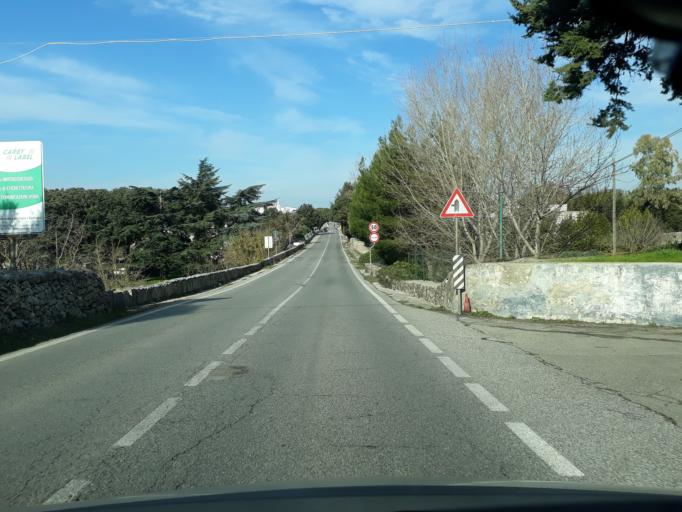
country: IT
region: Apulia
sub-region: Provincia di Bari
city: Locorotondo
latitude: 40.7304
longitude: 17.3326
